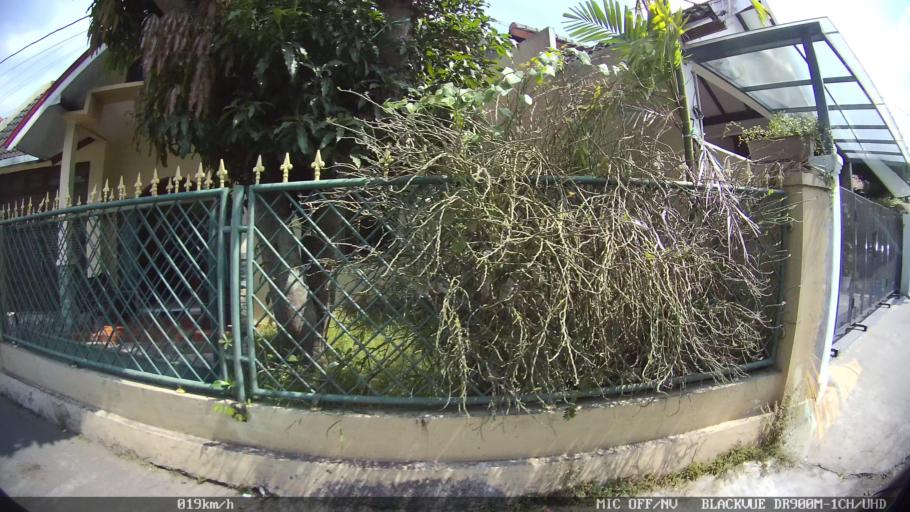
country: ID
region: Daerah Istimewa Yogyakarta
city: Yogyakarta
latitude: -7.8077
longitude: 110.4056
